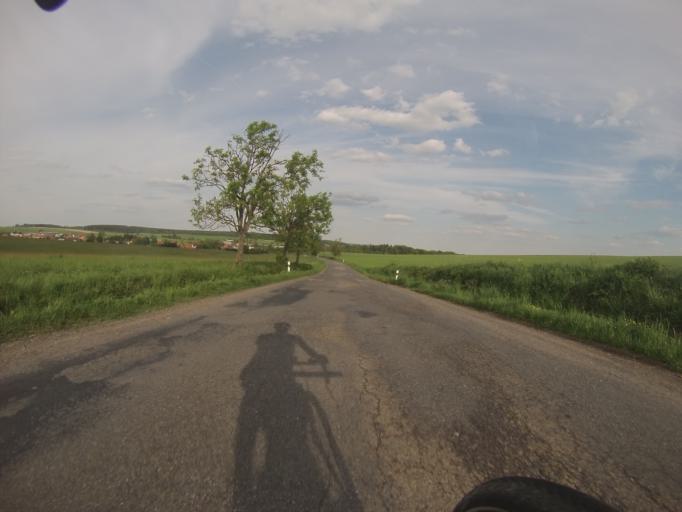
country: CZ
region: Olomoucky
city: Protivanov
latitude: 49.4390
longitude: 16.8452
